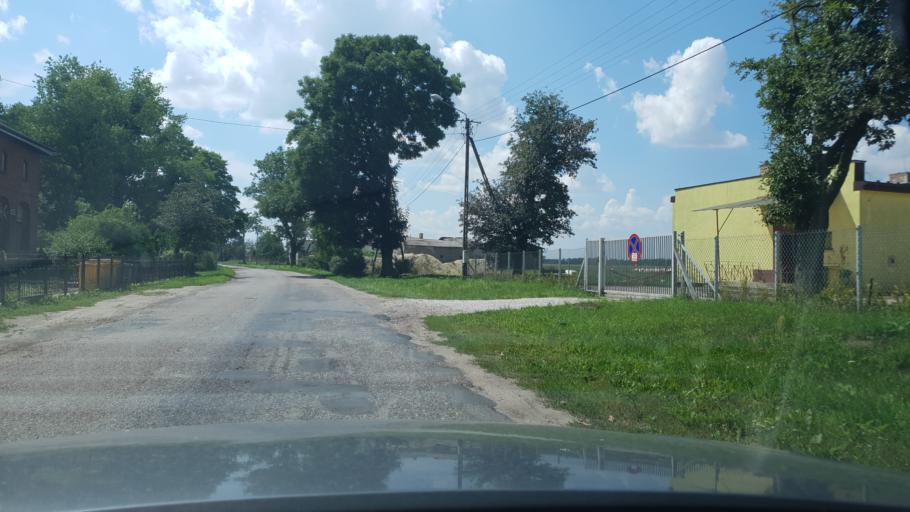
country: PL
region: Kujawsko-Pomorskie
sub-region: Powiat wabrzeski
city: Pluznica
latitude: 53.2641
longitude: 18.8352
